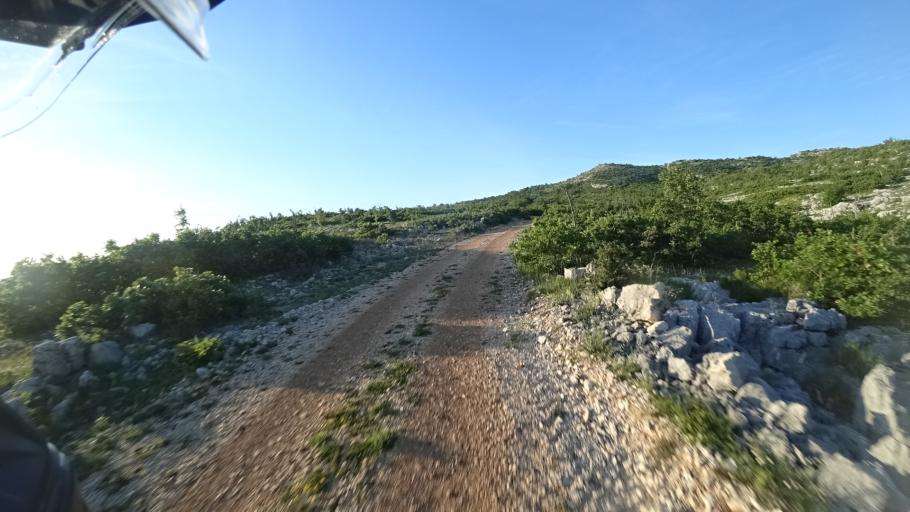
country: HR
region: Sibensko-Kniniska
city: Drnis
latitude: 43.8532
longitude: 16.3532
